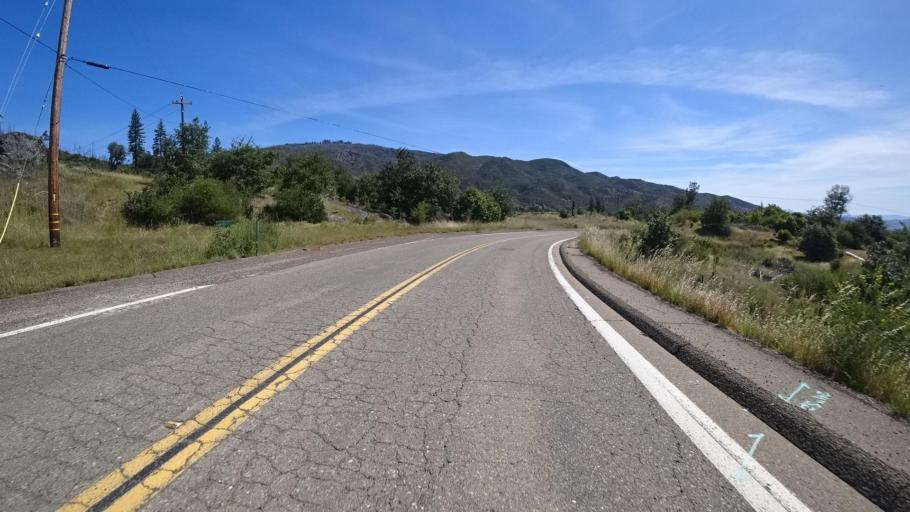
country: US
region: California
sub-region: Lake County
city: Cobb
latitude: 38.7830
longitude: -122.7019
